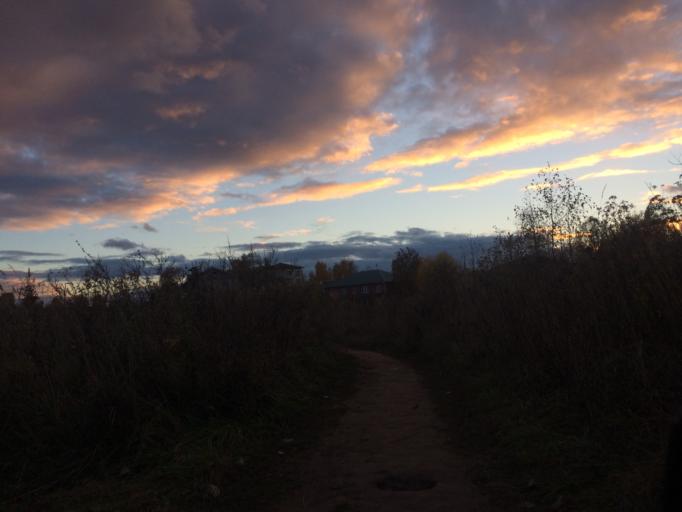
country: RU
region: Mariy-El
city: Yoshkar-Ola
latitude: 56.6182
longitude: 47.9114
